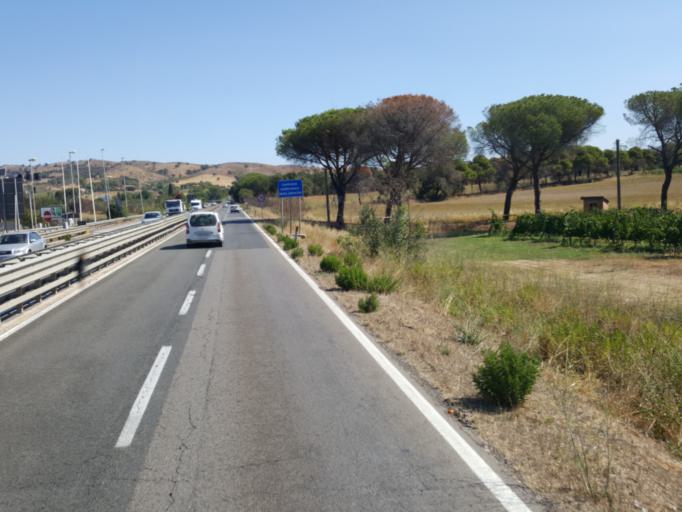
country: IT
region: Tuscany
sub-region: Provincia di Grosseto
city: Grosseto
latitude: 42.7075
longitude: 11.1408
